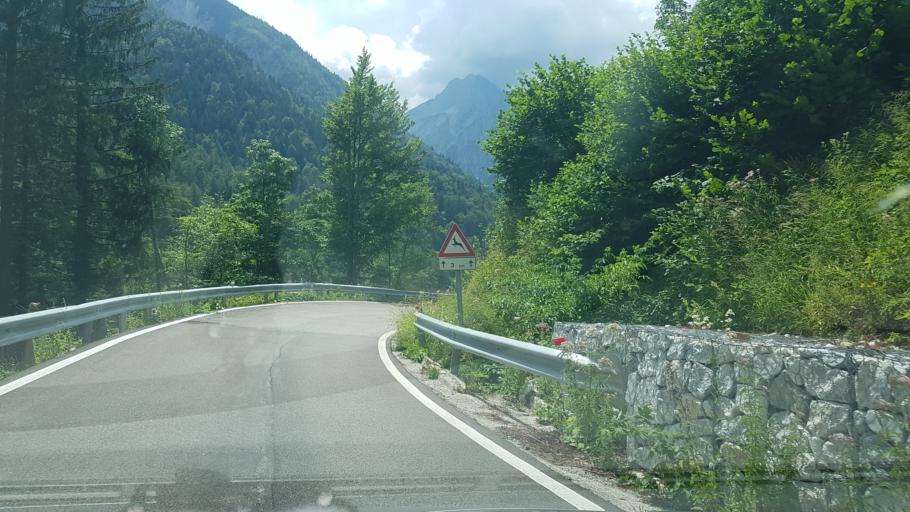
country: IT
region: Friuli Venezia Giulia
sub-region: Provincia di Udine
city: Pontebba
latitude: 46.4964
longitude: 13.2228
